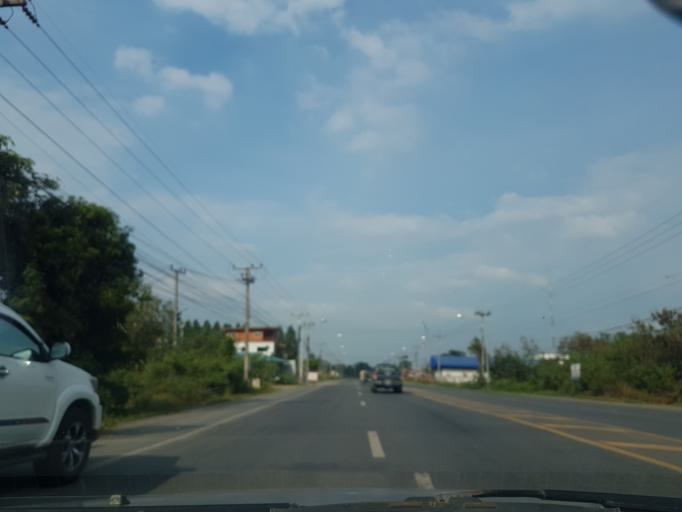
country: TH
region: Sara Buri
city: Ban Mo
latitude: 14.5973
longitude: 100.7338
